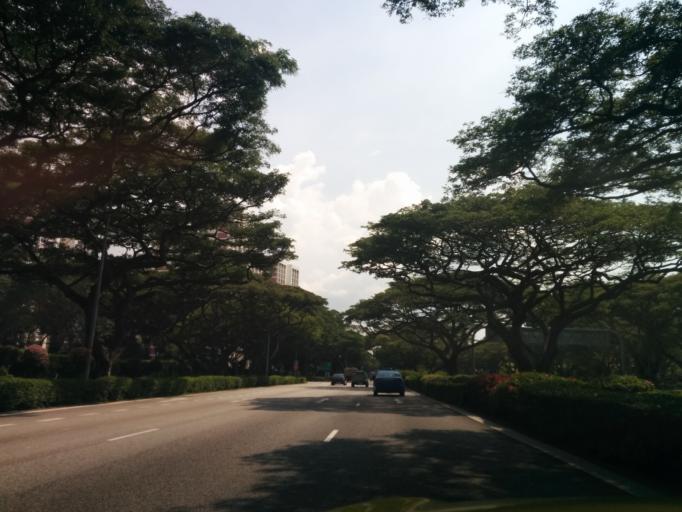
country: SG
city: Singapore
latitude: 1.3042
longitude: 103.9199
